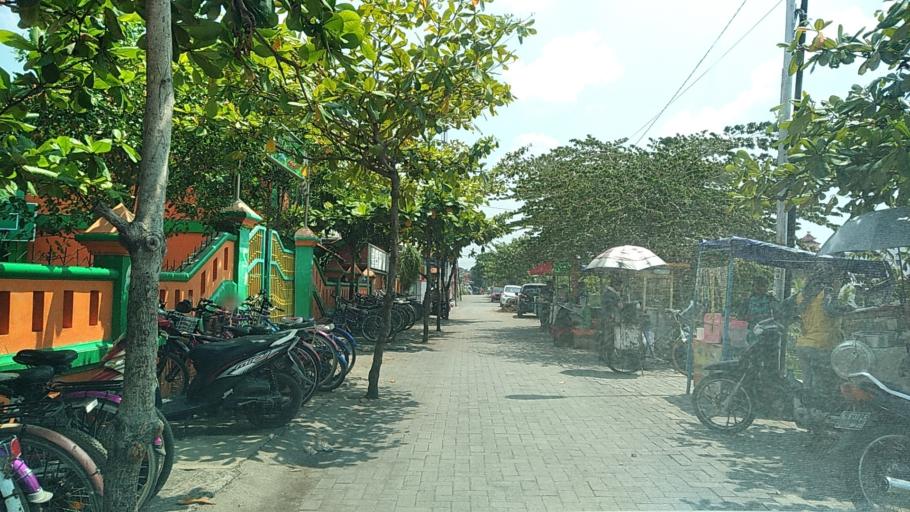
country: ID
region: Central Java
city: Semarang
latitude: -6.9648
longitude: 110.4406
